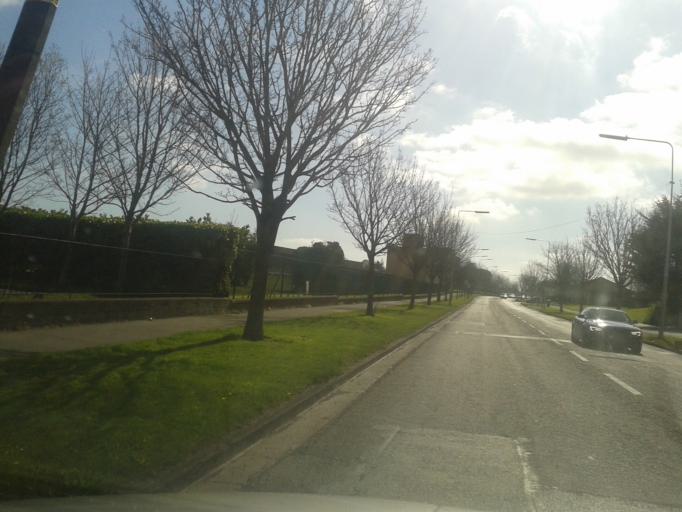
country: IE
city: Coolock
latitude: 53.3918
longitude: -6.2046
